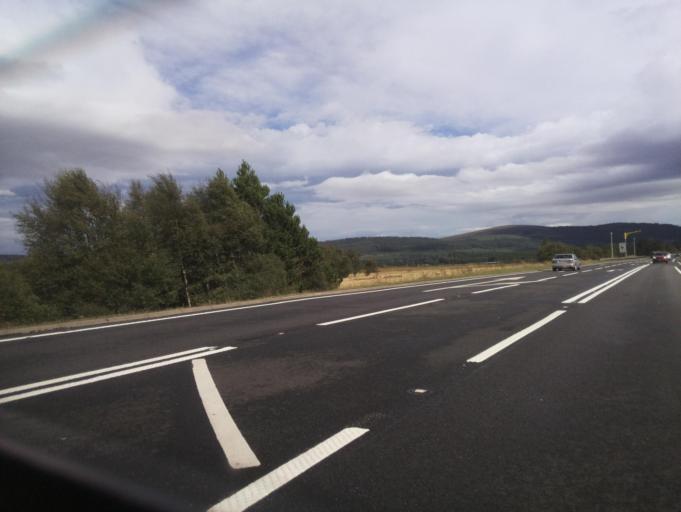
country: GB
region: Scotland
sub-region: Highland
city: Inverness
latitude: 57.3855
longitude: -4.0830
